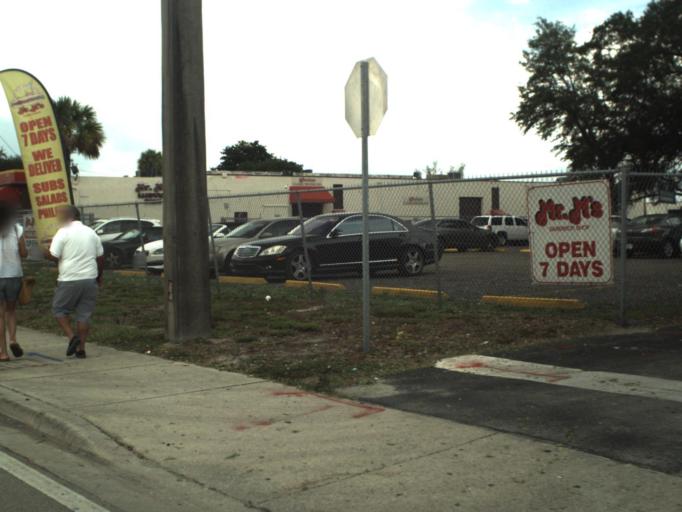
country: US
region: Florida
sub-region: Broward County
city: Dania Beach
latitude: 26.0481
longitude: -80.1656
